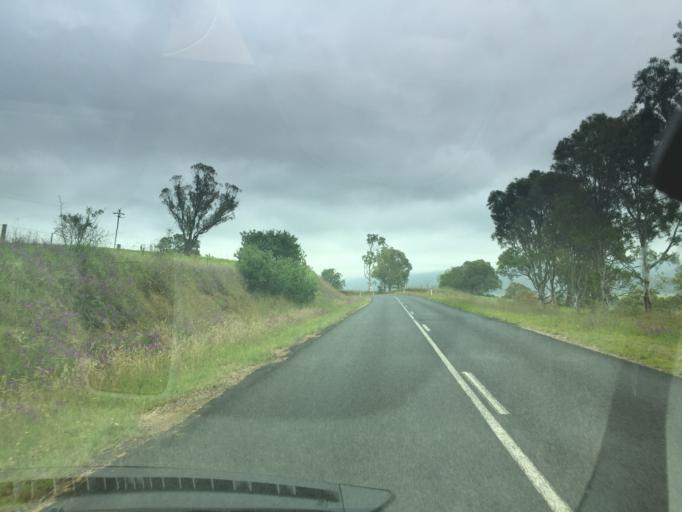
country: AU
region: New South Wales
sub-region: Bega Valley
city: Bega
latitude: -36.6611
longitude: 149.5827
